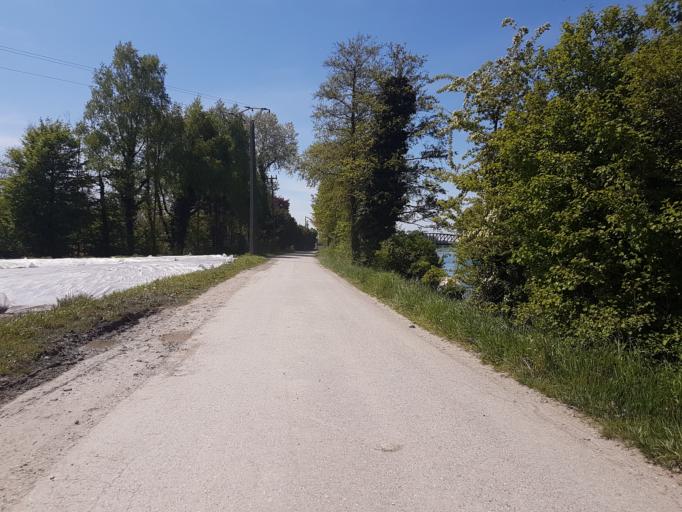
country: CH
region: Neuchatel
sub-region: Neuchatel District
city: Cornaux
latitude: 47.0128
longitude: 7.0325
